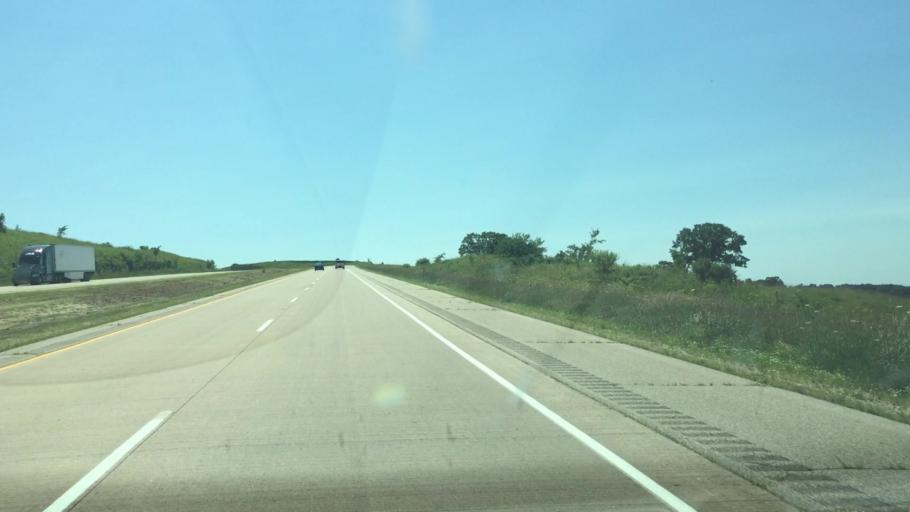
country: US
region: Wisconsin
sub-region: Iowa County
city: Mineral Point
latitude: 42.8091
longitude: -90.2642
